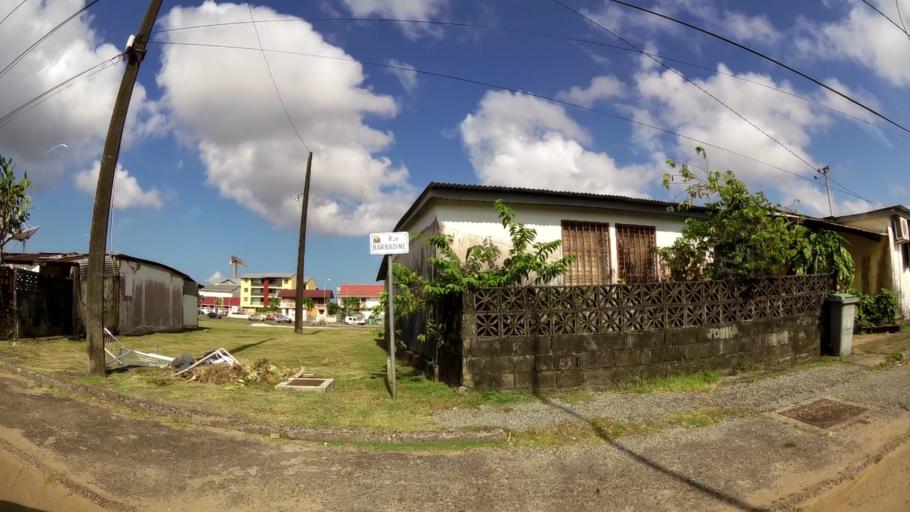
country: GF
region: Guyane
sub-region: Guyane
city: Cayenne
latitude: 4.9344
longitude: -52.3255
